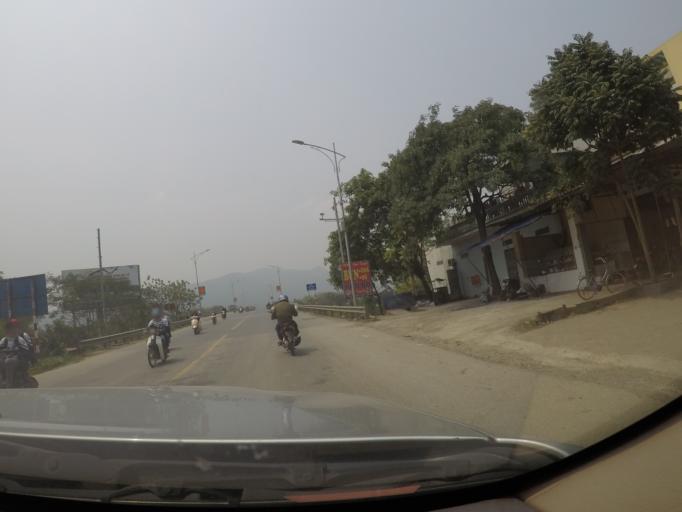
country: VN
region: Thanh Hoa
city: Thi Tran Cam Thuy
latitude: 20.2143
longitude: 105.4833
